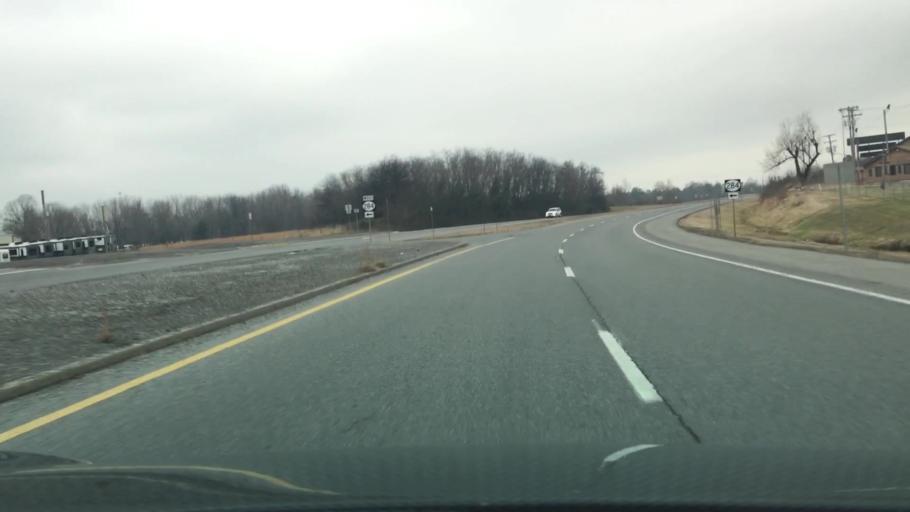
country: US
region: Kentucky
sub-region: McCracken County
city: Reidland
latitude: 36.9897
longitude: -88.5051
